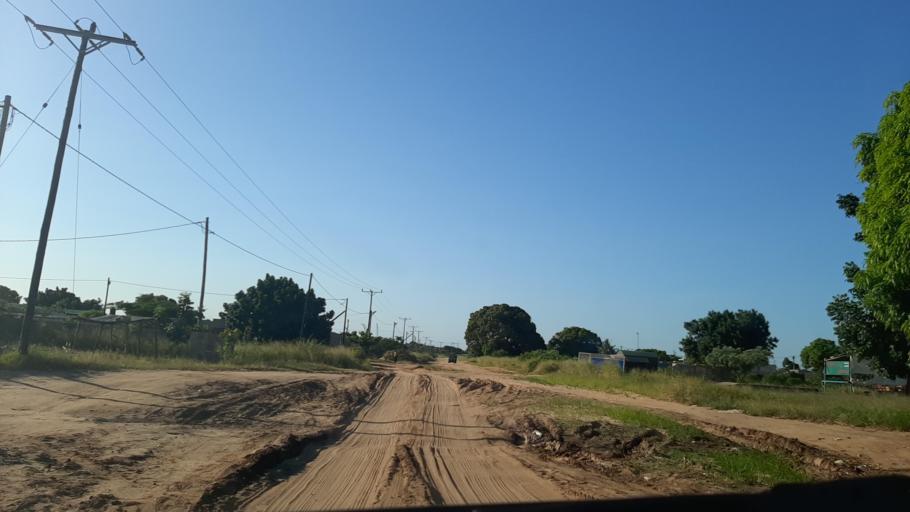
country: MZ
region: Maputo City
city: Maputo
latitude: -25.7695
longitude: 32.5483
